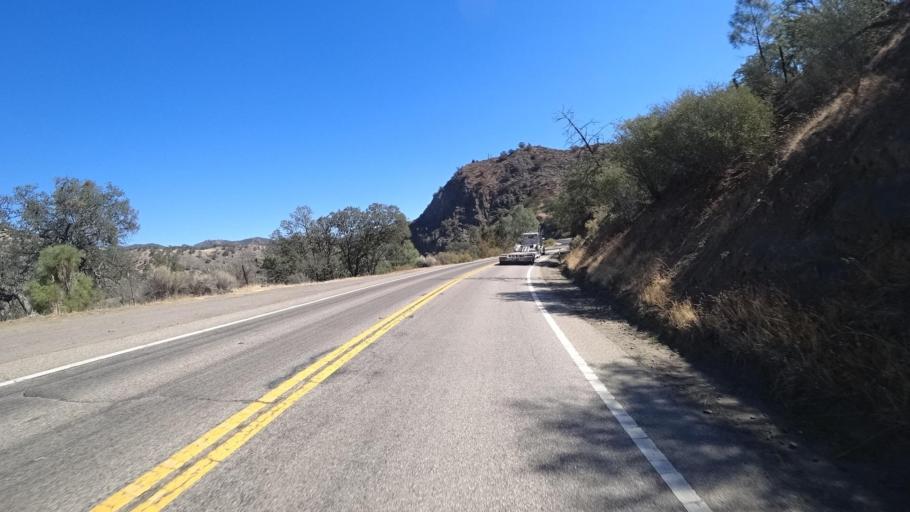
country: US
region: California
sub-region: Fresno County
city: Coalinga
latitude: 36.1992
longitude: -120.7389
